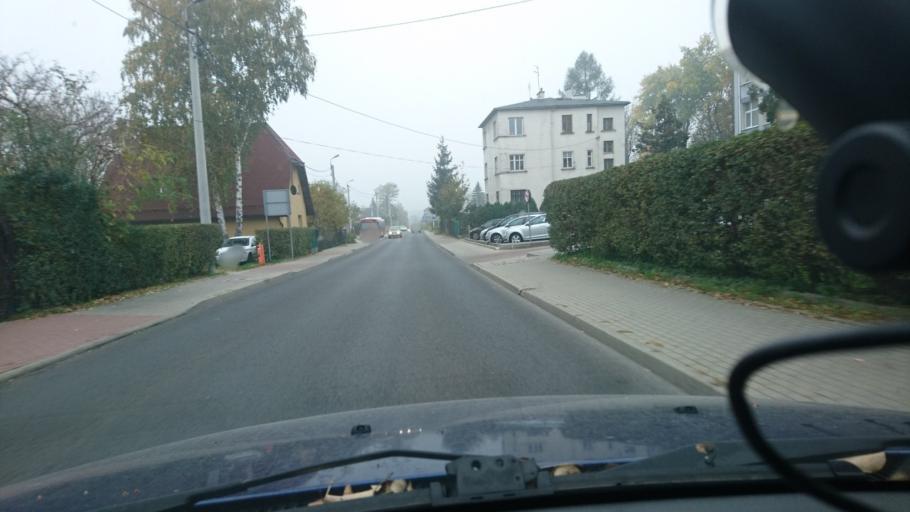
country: PL
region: Silesian Voivodeship
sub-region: Bielsko-Biala
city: Bielsko-Biala
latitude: 49.8200
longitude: 19.0308
